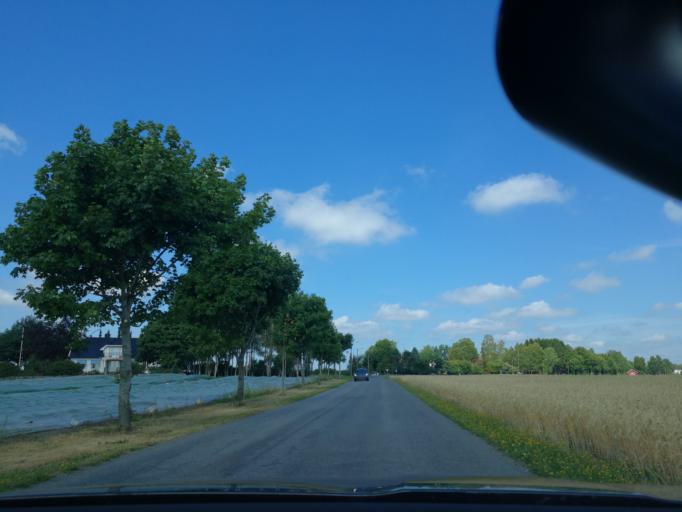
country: NO
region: Vestfold
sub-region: Sandefjord
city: Sandefjord
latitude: 59.1543
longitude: 10.2015
